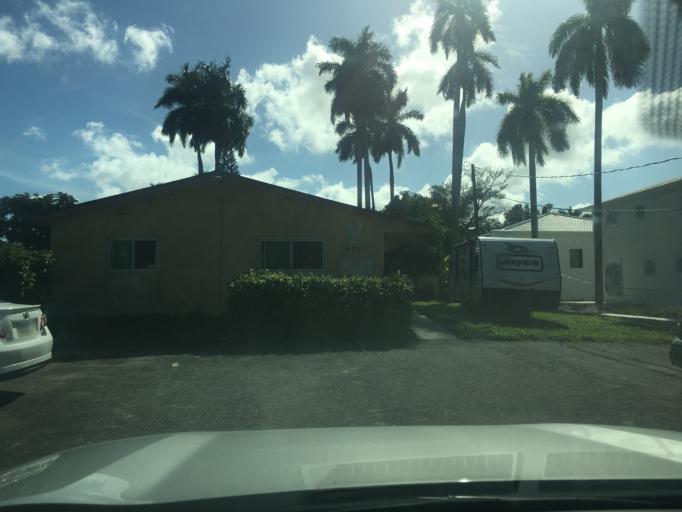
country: US
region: Florida
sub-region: Broward County
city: Broadview Park
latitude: 26.0667
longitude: -80.1863
